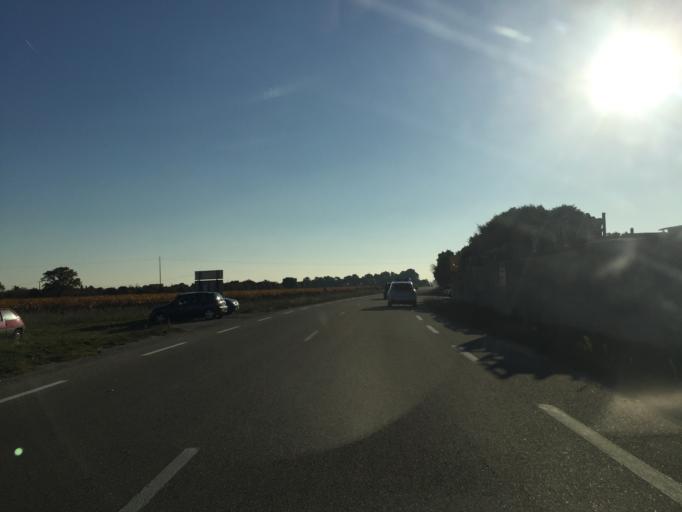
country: FR
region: Provence-Alpes-Cote d'Azur
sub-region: Departement du Vaucluse
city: Sainte-Cecile-les-Vignes
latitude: 44.2307
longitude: 4.8807
